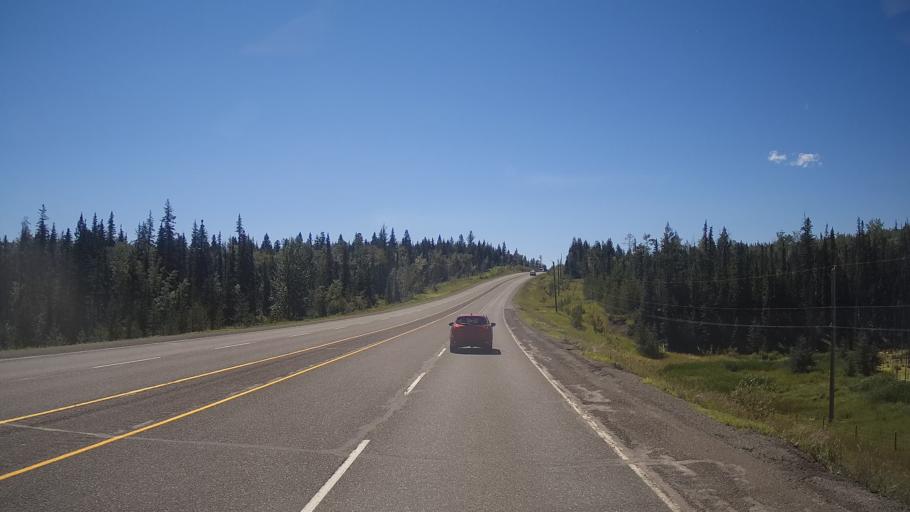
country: CA
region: British Columbia
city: Cache Creek
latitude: 51.4901
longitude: -121.3687
